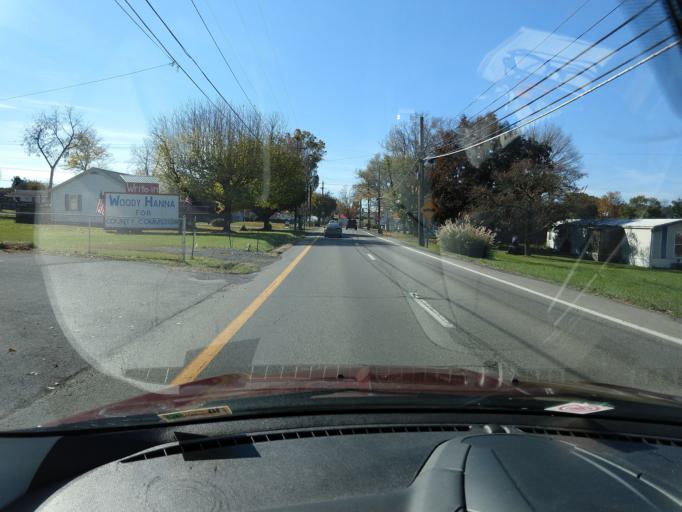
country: US
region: West Virginia
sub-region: Greenbrier County
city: Fairlea
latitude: 37.7815
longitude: -80.4586
